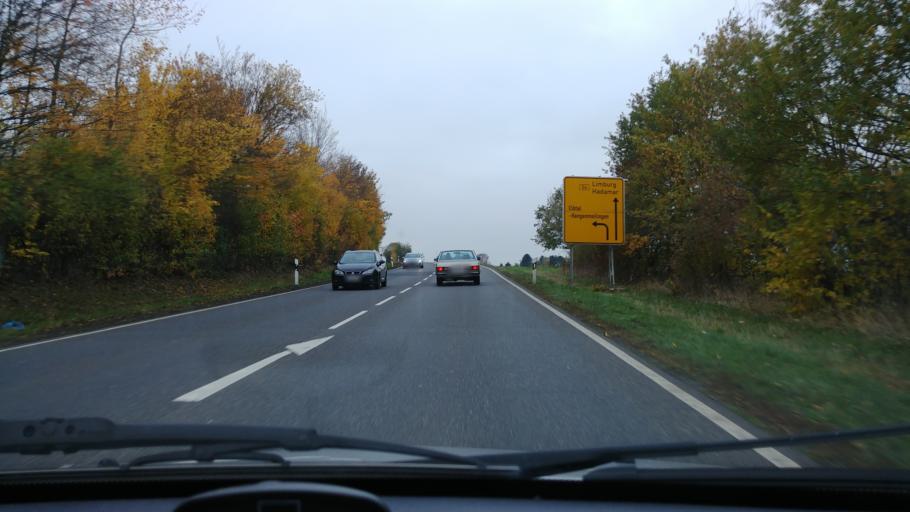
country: DE
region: Hesse
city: Waldbrunn
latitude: 50.4925
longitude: 8.0620
